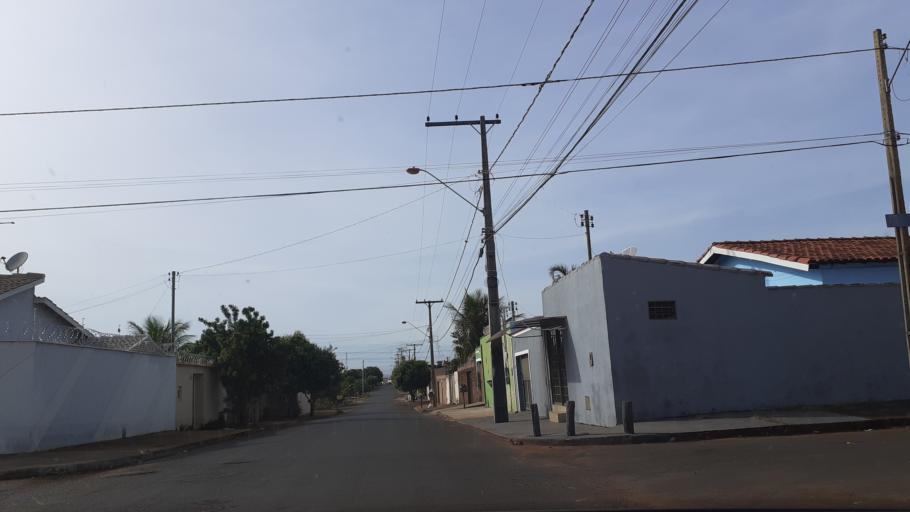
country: BR
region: Goias
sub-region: Itumbiara
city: Itumbiara
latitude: -18.4178
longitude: -49.2495
